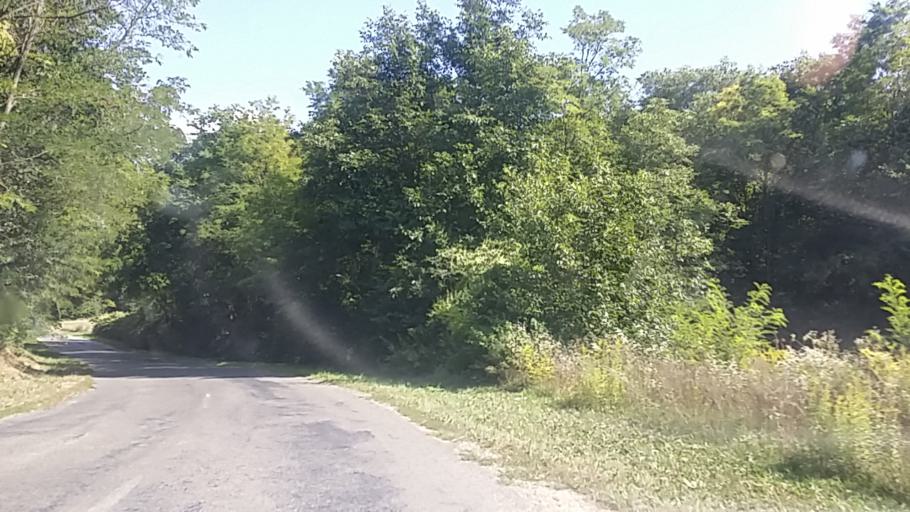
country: HU
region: Tolna
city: Gyonk
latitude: 46.5371
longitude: 18.4604
